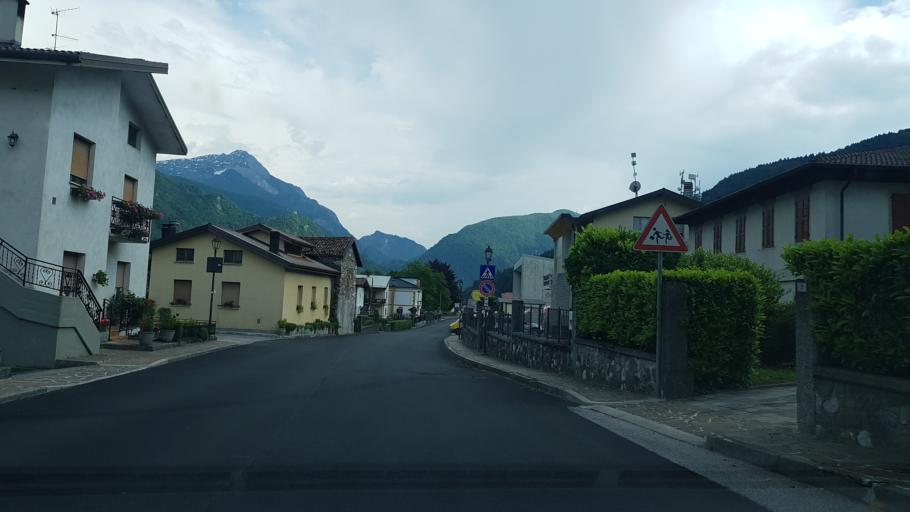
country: IT
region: Friuli Venezia Giulia
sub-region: Provincia di Udine
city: Zuglio
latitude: 46.4614
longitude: 13.0262
